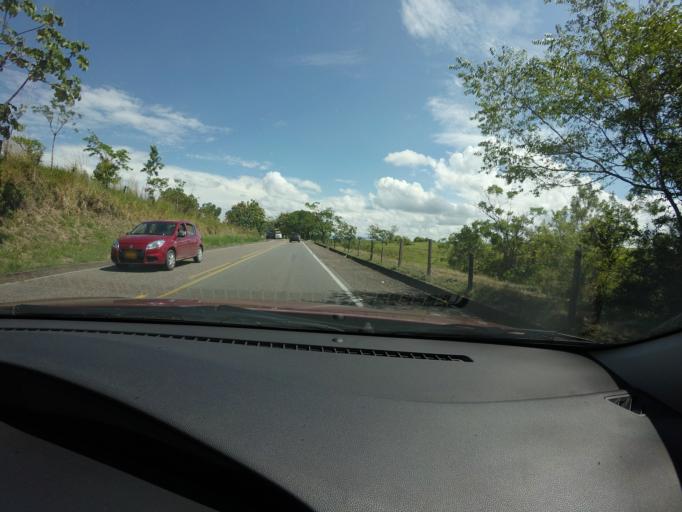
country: CO
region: Antioquia
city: Puerto Triunfo
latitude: 5.9007
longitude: -74.6342
